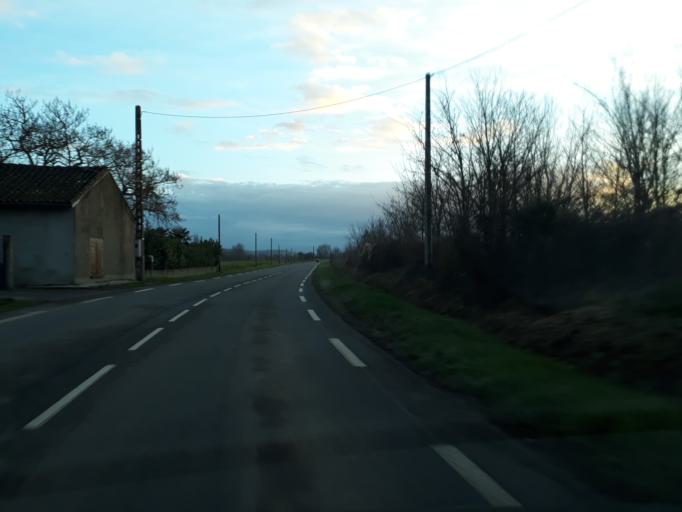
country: FR
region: Midi-Pyrenees
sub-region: Departement de la Haute-Garonne
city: Marquefave
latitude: 43.3336
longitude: 1.2506
